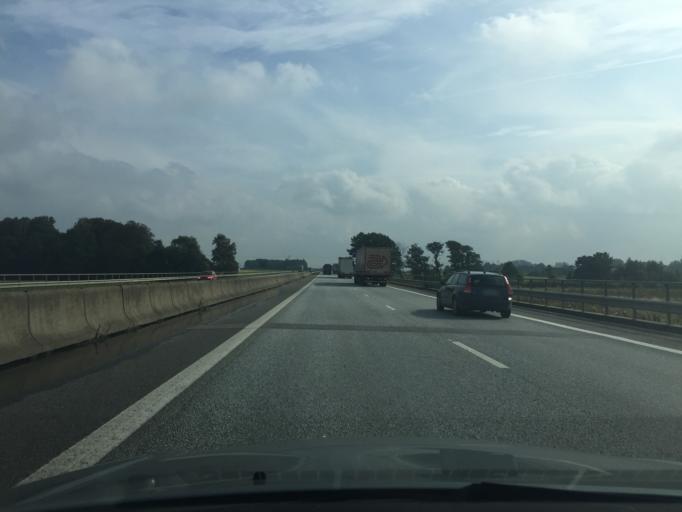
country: SE
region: Skane
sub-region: Kavlinge Kommun
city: Loddekopinge
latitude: 55.7504
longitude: 13.0123
